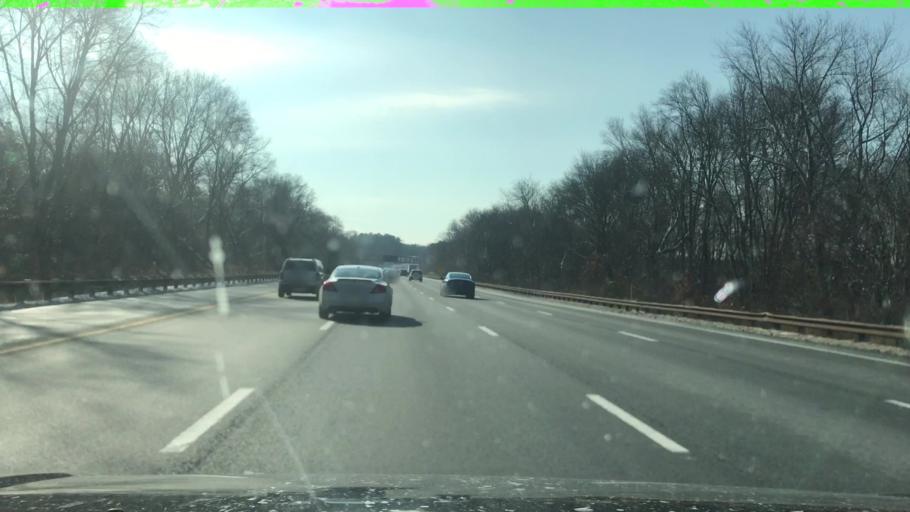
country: US
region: New Jersey
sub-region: Monmouth County
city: Ramtown
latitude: 40.1442
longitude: -74.1109
